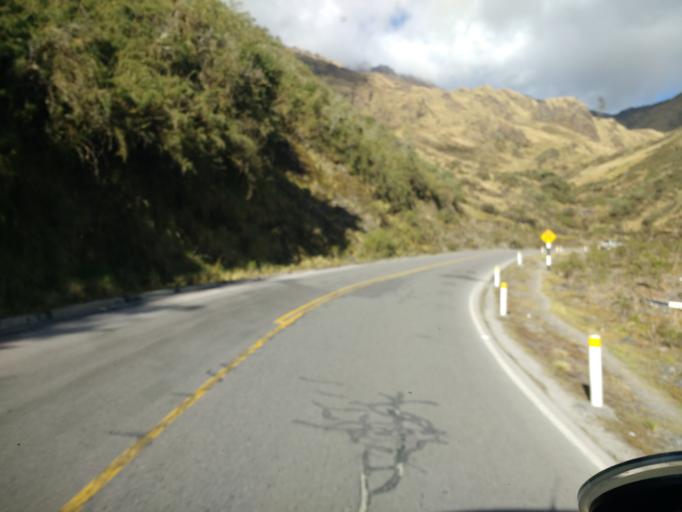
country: PE
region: Cusco
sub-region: Provincia de Urubamba
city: Ollantaytambo
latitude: -13.1207
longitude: -72.3268
